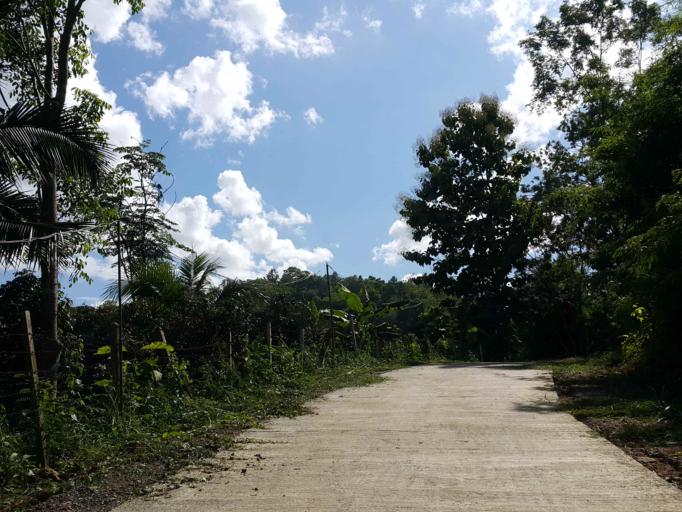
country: TH
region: Chiang Mai
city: Mae Taeng
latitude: 18.9637
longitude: 98.8862
